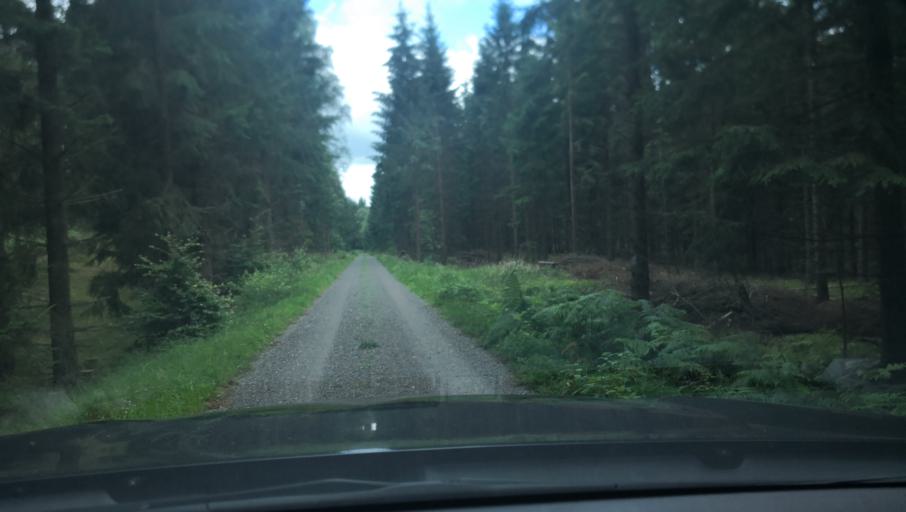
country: SE
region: Skane
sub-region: Simrishamns Kommun
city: Kivik
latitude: 55.6094
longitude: 14.1195
